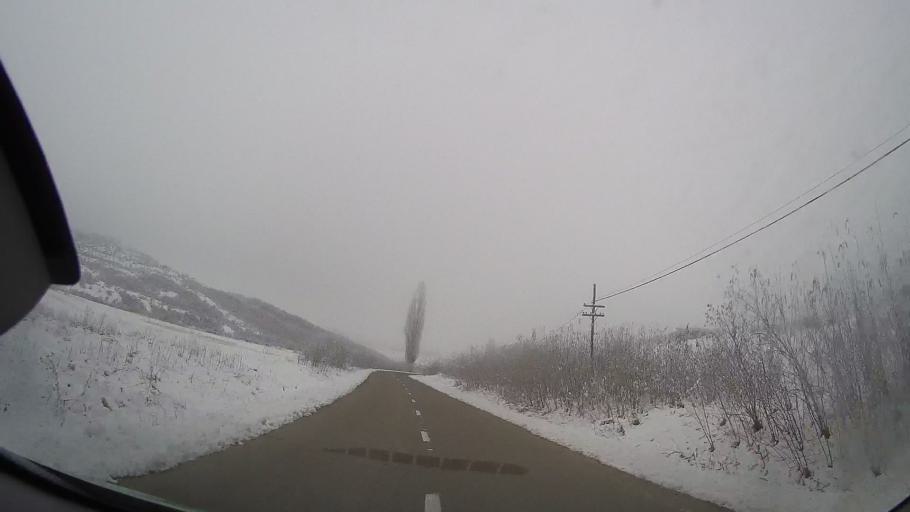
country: RO
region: Neamt
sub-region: Comuna Valea Ursului
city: Valea Ursului
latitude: 46.8021
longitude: 27.1100
